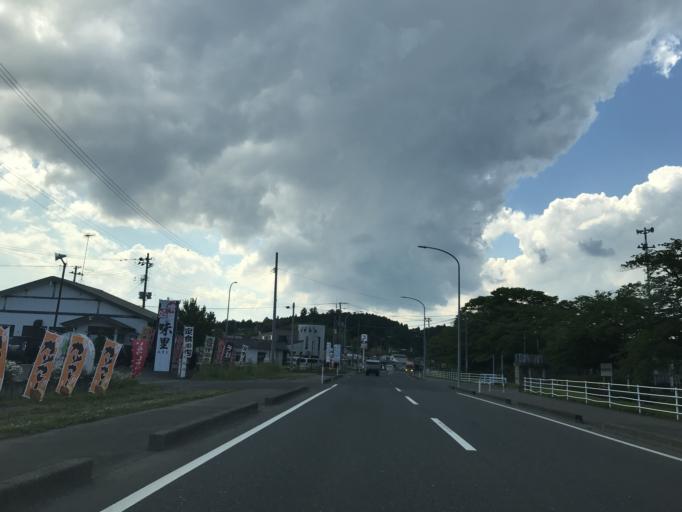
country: JP
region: Miyagi
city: Wakuya
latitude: 38.5438
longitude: 141.1449
